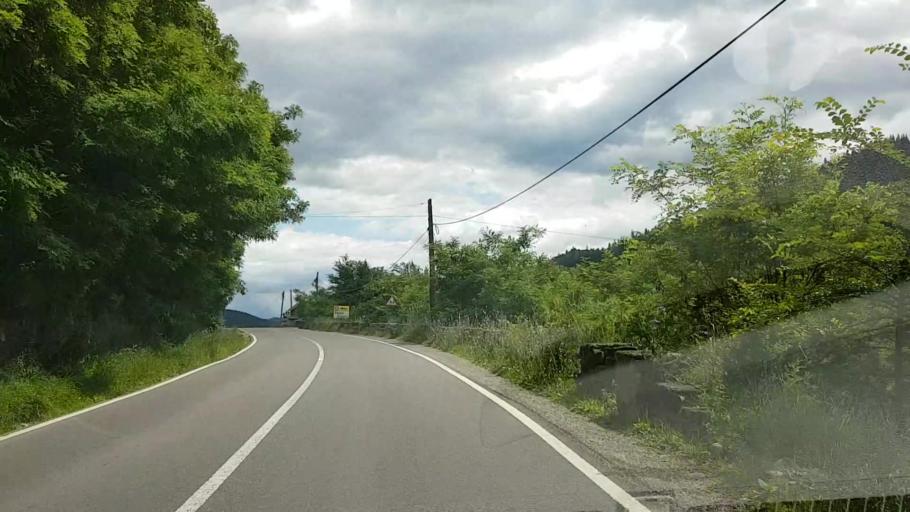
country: RO
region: Neamt
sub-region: Comuna Poiana Teiului
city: Poiana Teiului
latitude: 47.1208
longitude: 25.9113
